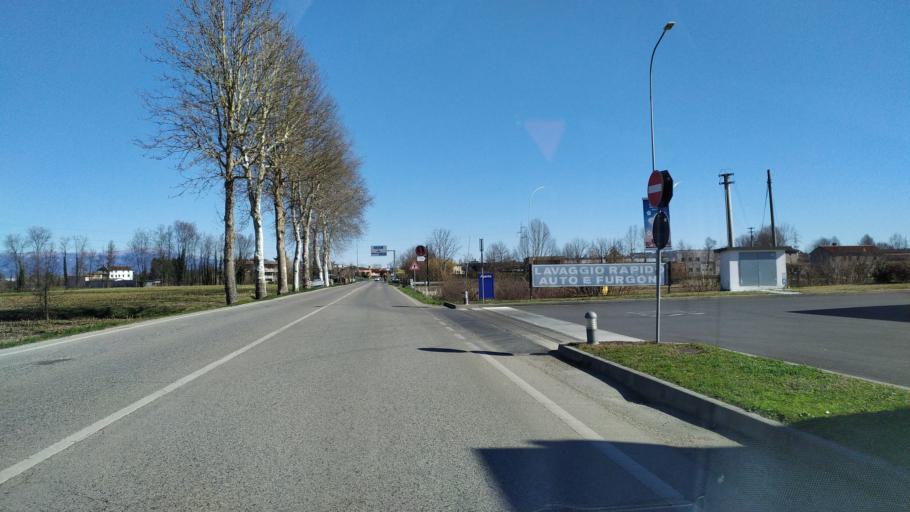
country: IT
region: Veneto
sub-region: Provincia di Vicenza
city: Monticello Conte Otto
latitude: 45.6086
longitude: 11.5591
